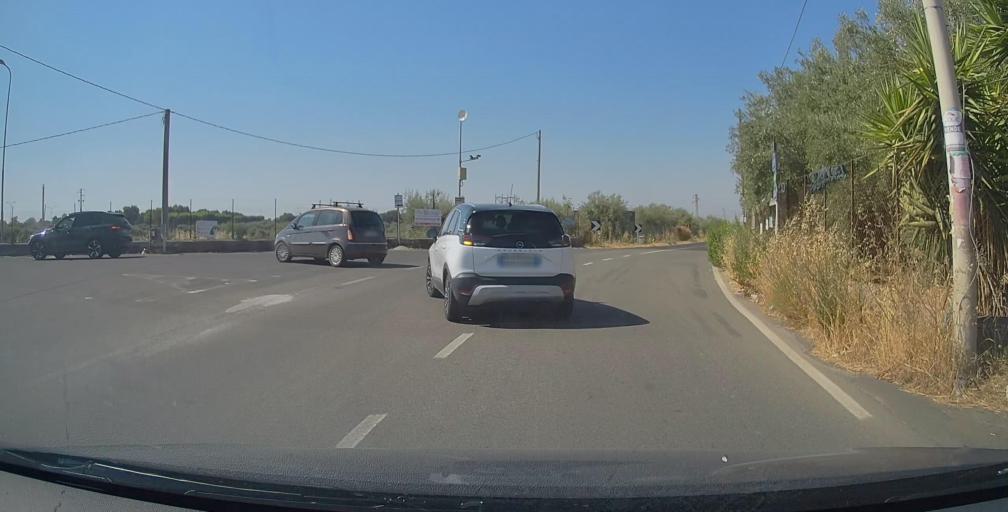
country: IT
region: Sicily
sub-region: Catania
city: Palazzolo
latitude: 37.5416
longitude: 14.9299
